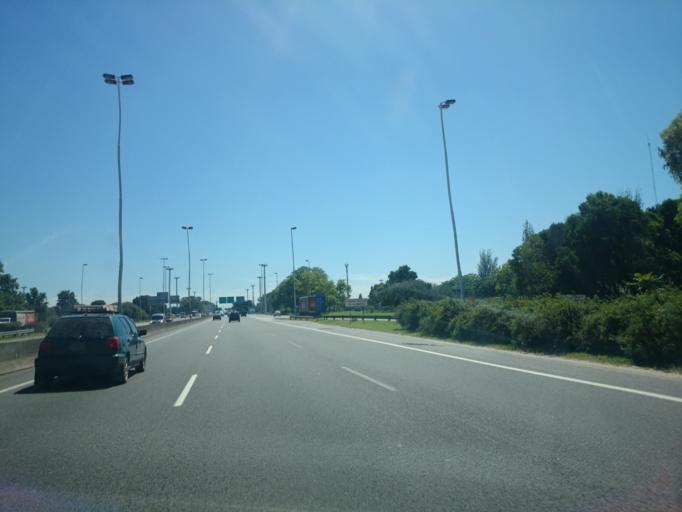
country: AR
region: Buenos Aires F.D.
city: Villa Lugano
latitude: -34.6908
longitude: -58.4885
